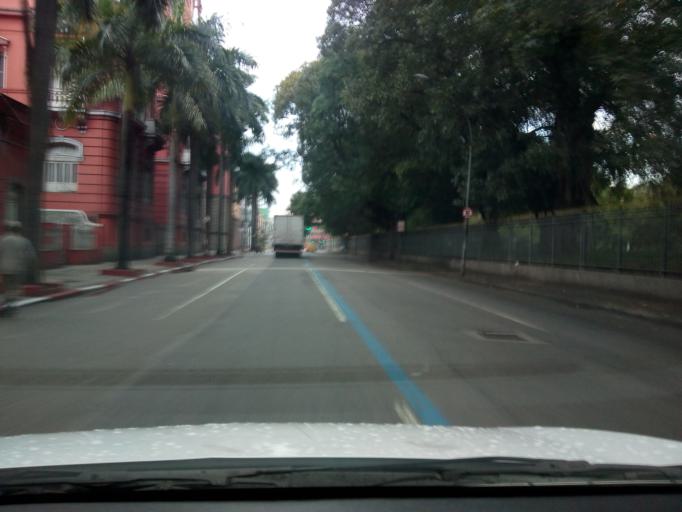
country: BR
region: Rio de Janeiro
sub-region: Rio De Janeiro
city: Rio de Janeiro
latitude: -22.9084
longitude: -43.1869
